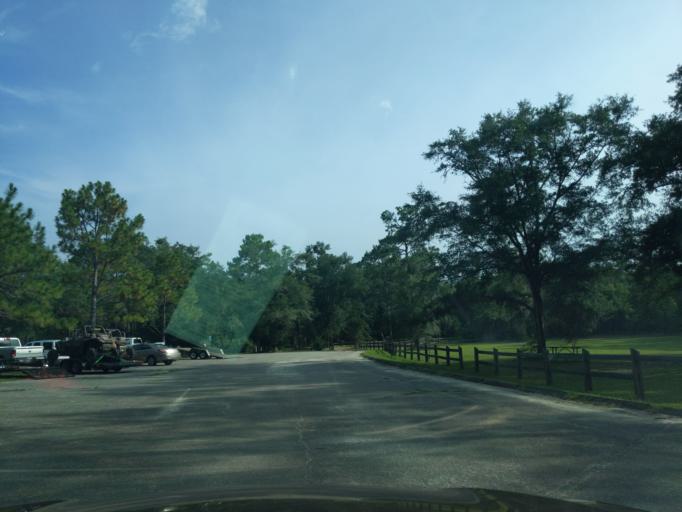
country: US
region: Florida
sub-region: Gadsden County
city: Midway
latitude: 30.4036
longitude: -84.4081
